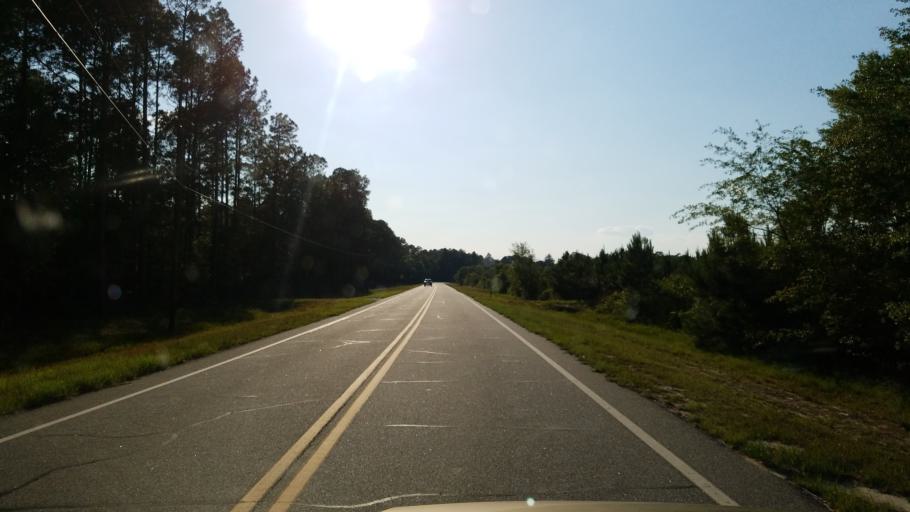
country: US
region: Georgia
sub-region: Lanier County
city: Lakeland
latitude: 30.9034
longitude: -83.0718
